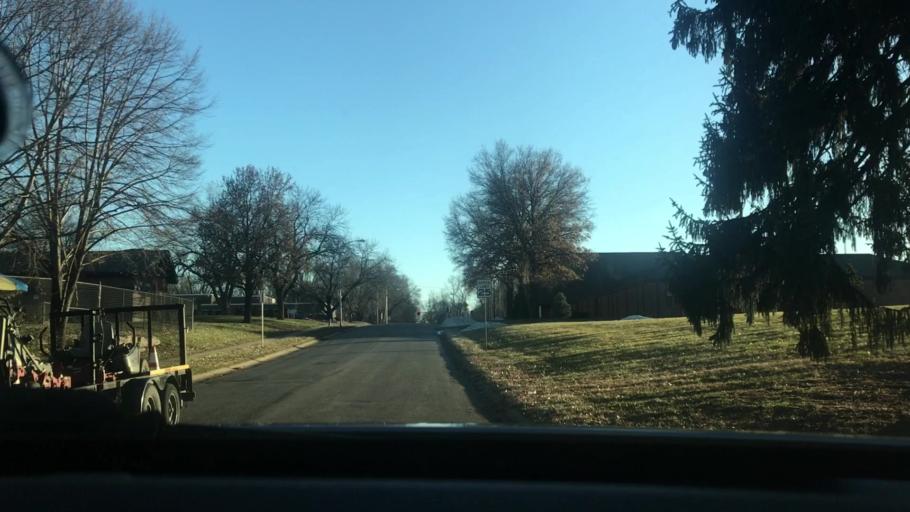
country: US
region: Kansas
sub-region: Johnson County
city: Overland Park
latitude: 38.9950
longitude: -94.6736
